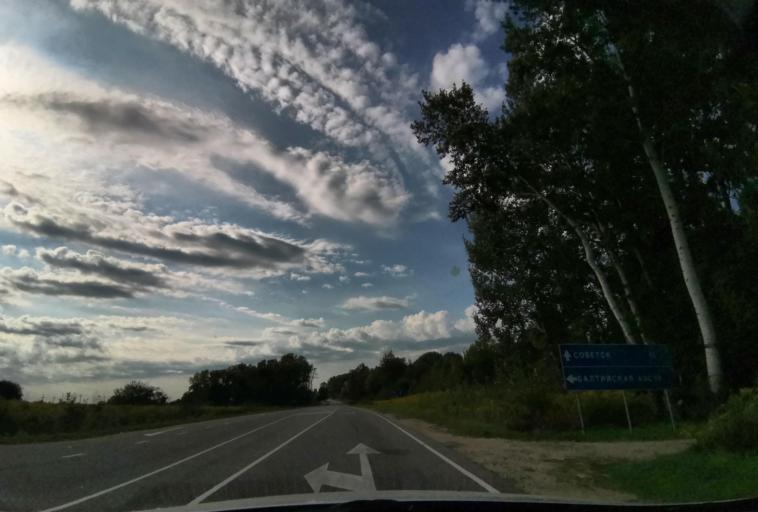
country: RU
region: Kaliningrad
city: Neman
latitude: 55.0198
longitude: 22.0846
